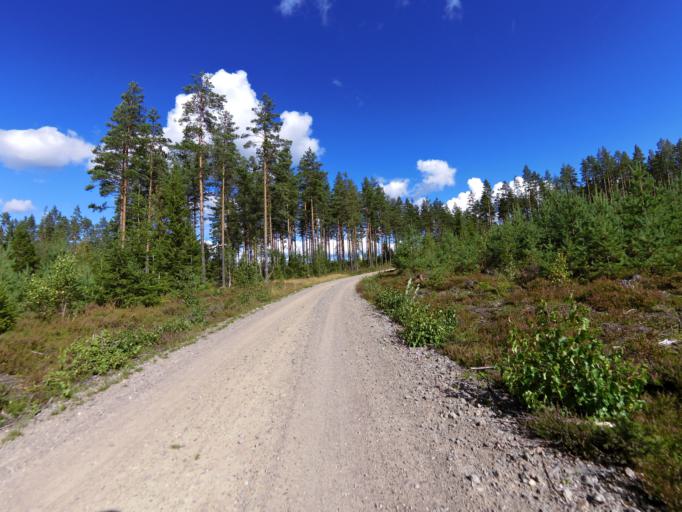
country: SE
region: Gaevleborg
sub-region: Ockelbo Kommun
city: Ockelbo
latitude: 60.8390
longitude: 16.7624
